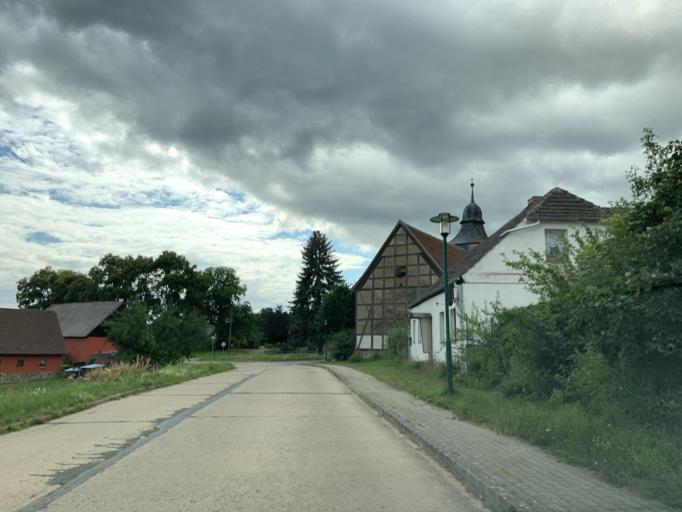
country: DE
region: Mecklenburg-Vorpommern
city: Carpin
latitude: 53.3782
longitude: 13.1818
